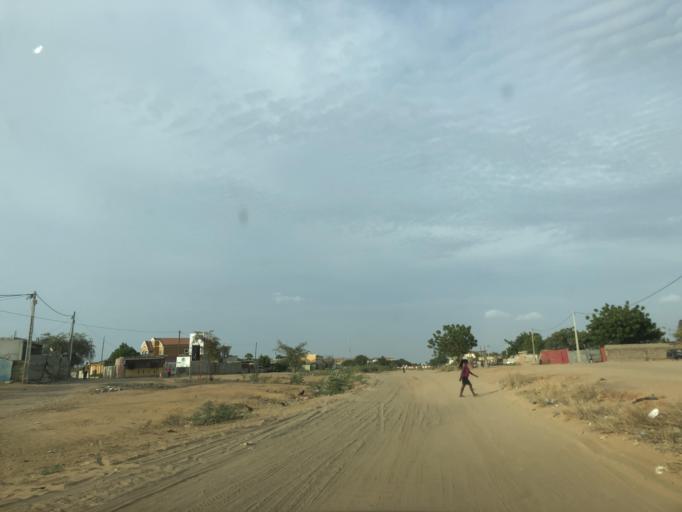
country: AO
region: Luanda
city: Luanda
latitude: -8.9170
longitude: 13.3108
